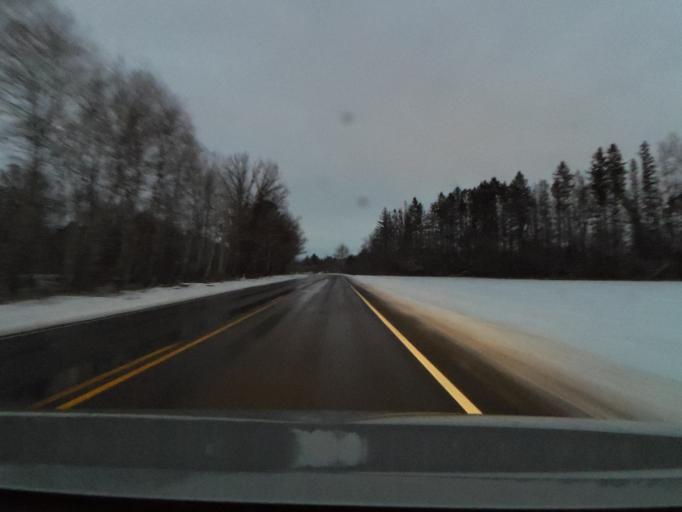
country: US
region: Wisconsin
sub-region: Dunn County
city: Menomonie
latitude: 44.9197
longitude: -91.9587
